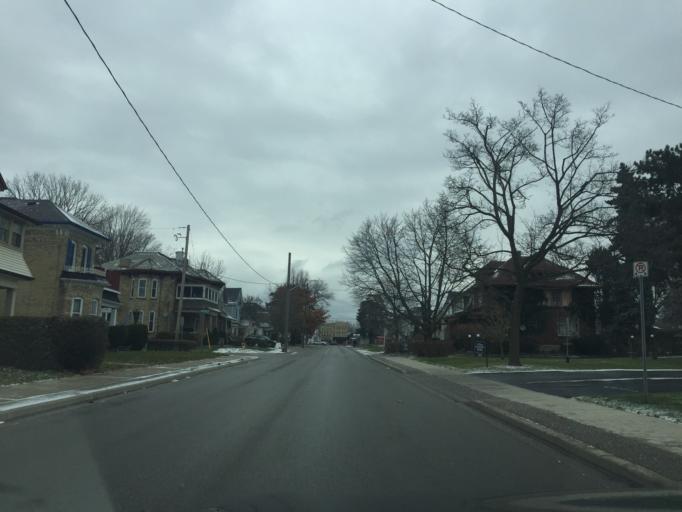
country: CA
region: Ontario
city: St. Thomas
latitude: 42.7761
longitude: -81.1985
